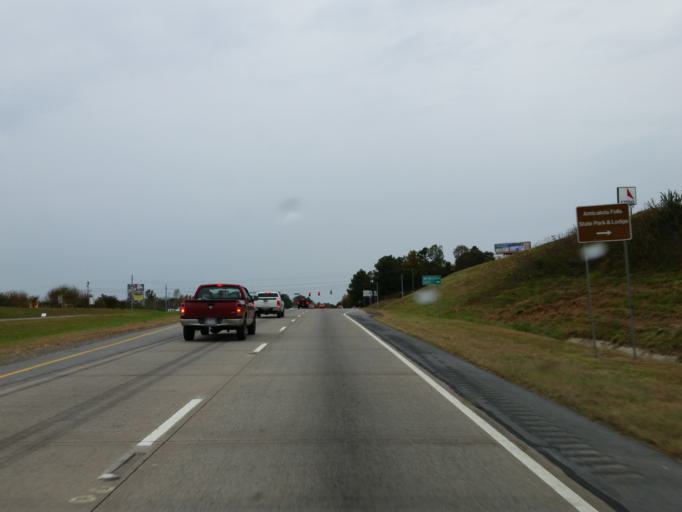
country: US
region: Georgia
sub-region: Pickens County
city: Nelson
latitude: 34.4052
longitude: -84.4203
